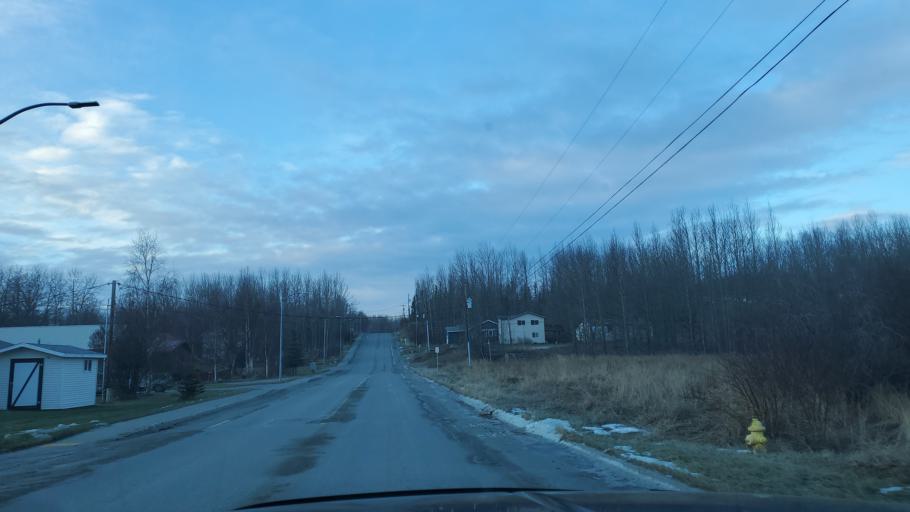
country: US
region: Alaska
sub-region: Matanuska-Susitna Borough
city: Palmer
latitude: 61.6139
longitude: -149.1084
